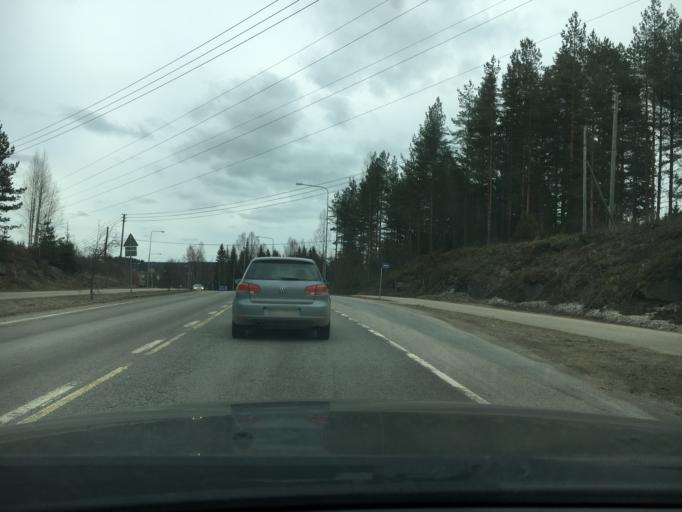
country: FI
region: Central Finland
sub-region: AEaenekoski
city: Suolahti
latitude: 62.5630
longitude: 25.8381
